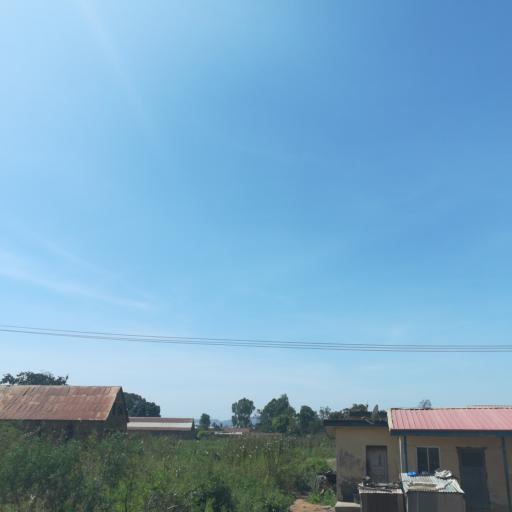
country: NG
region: Plateau
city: Bukuru
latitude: 9.7884
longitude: 8.8737
